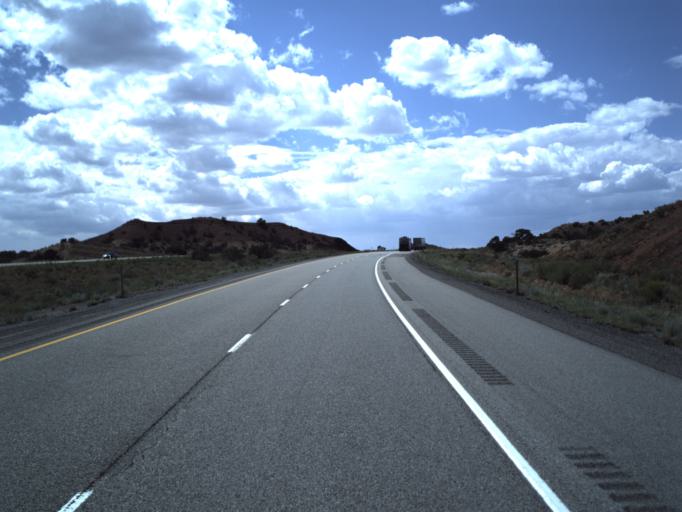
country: US
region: Utah
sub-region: Emery County
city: Castle Dale
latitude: 38.8678
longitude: -110.7054
